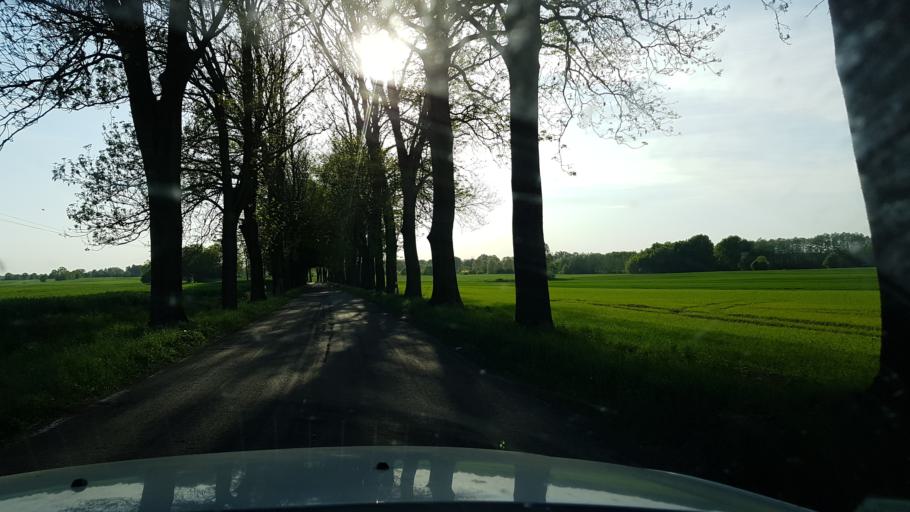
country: PL
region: West Pomeranian Voivodeship
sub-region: Powiat lobeski
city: Dobra
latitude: 53.5761
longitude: 15.2562
